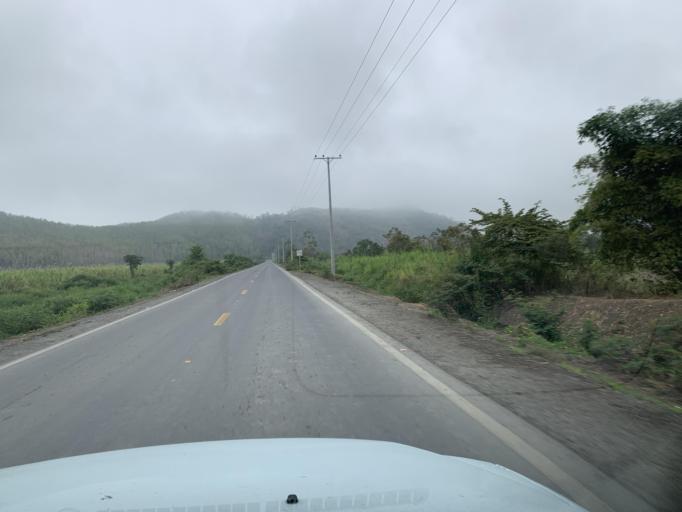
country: EC
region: Guayas
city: Coronel Marcelino Mariduena
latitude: -2.3467
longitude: -79.5294
